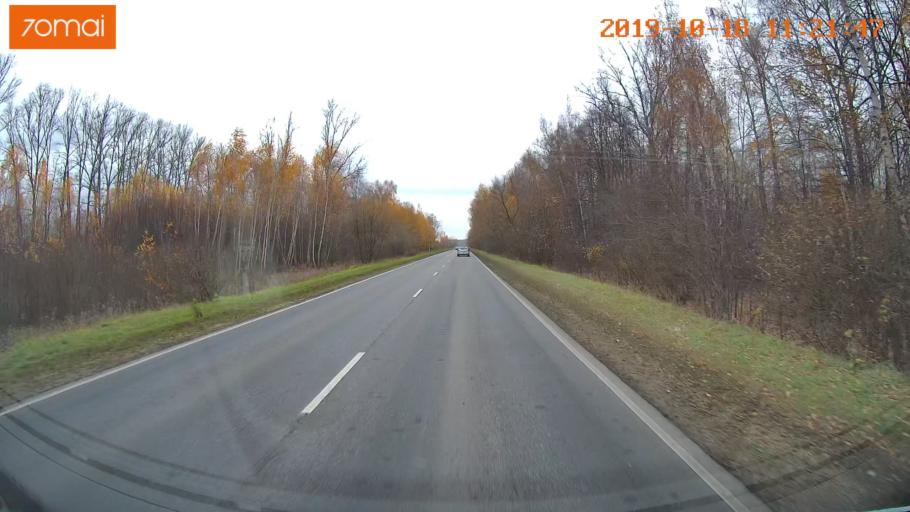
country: RU
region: Tula
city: Kimovsk
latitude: 54.0786
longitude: 38.5705
